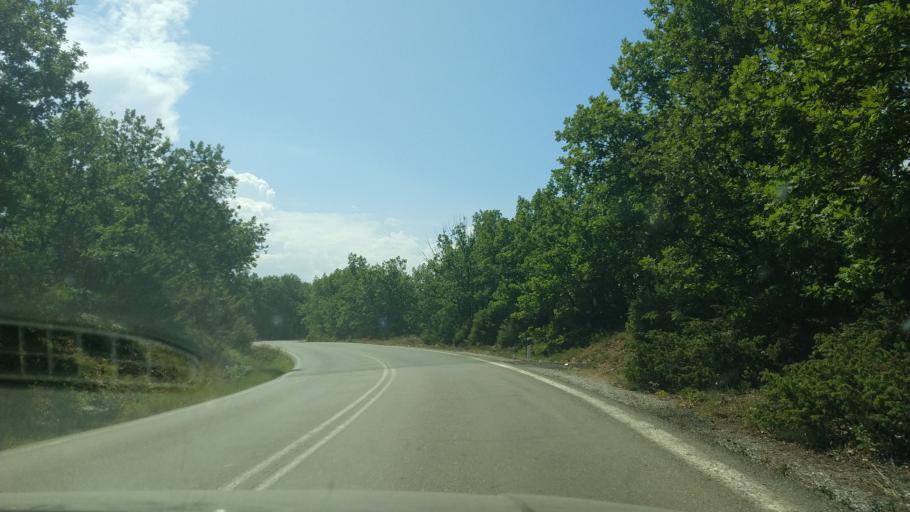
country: GR
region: West Macedonia
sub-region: Nomos Grevenon
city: Grevena
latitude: 40.0667
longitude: 21.4508
